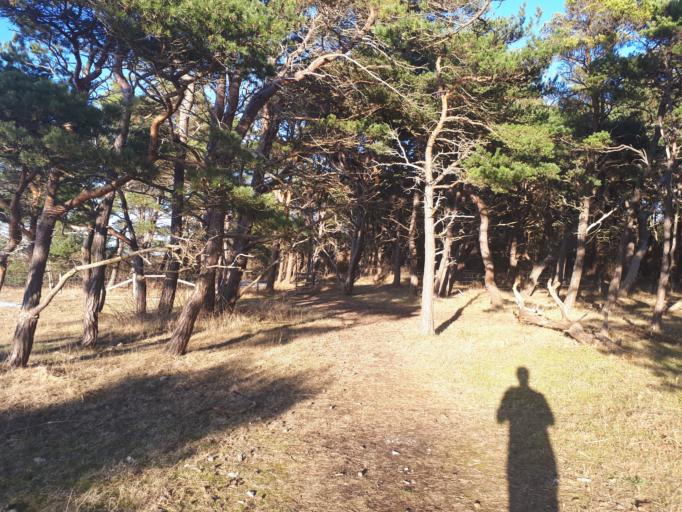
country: SE
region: Gotland
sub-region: Gotland
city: Visby
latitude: 57.6882
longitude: 18.3468
